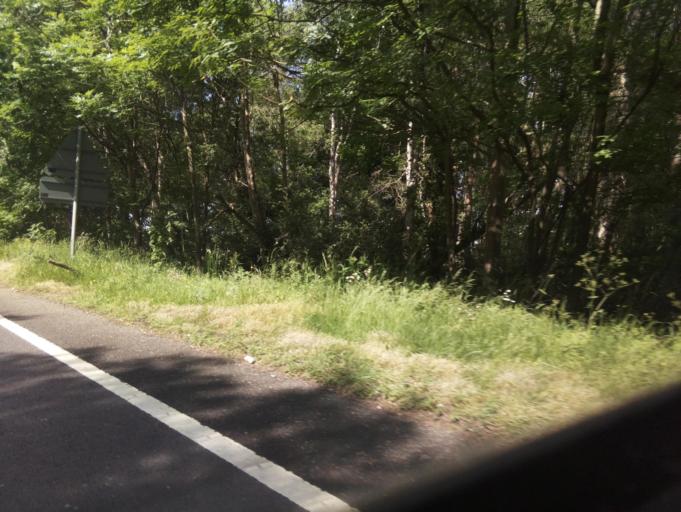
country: GB
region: England
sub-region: Lincolnshire
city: Skellingthorpe
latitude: 53.2198
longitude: -0.6153
